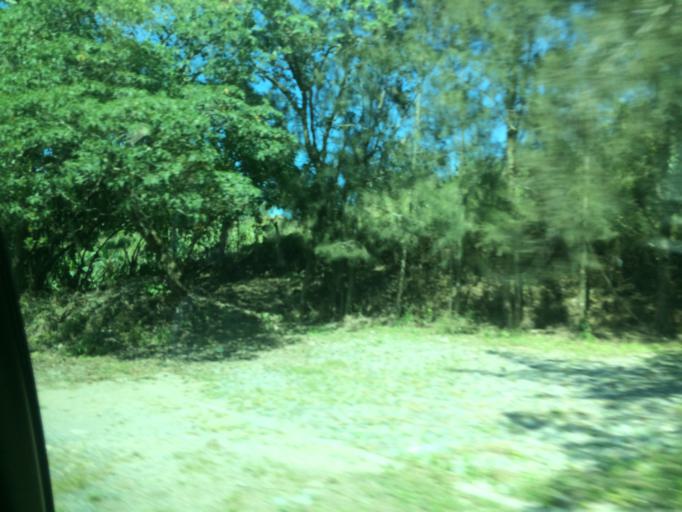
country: MX
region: Colima
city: Suchitlan
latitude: 19.4248
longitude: -103.6898
